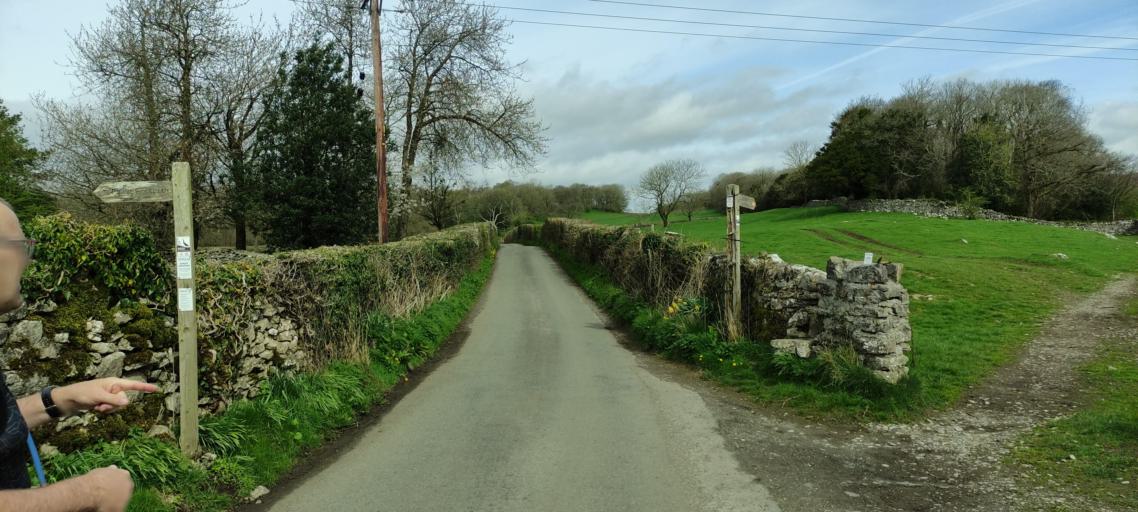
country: GB
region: England
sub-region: Cumbria
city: Arnside
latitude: 54.2037
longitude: -2.8025
